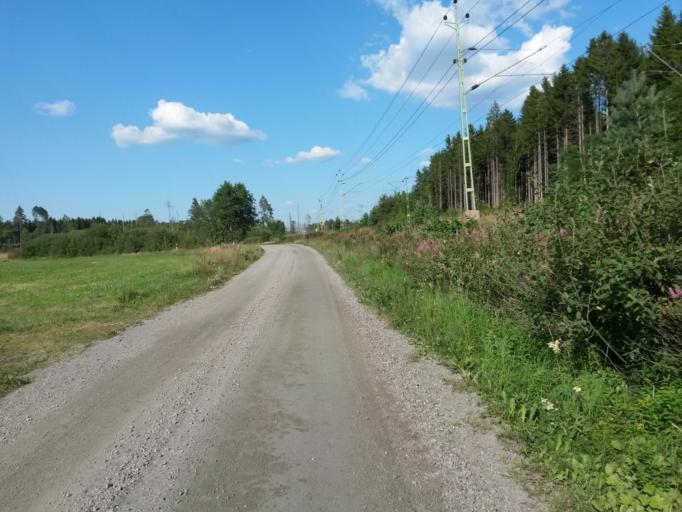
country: SE
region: Vaestra Goetaland
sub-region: Vargarda Kommun
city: Jonstorp
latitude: 58.0216
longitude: 12.7351
